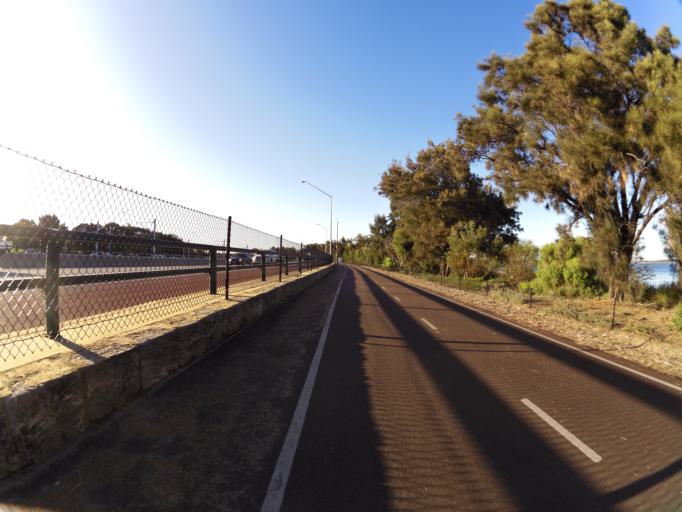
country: AU
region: Western Australia
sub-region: South Perth
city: South Perth
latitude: -31.9778
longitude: 115.8480
